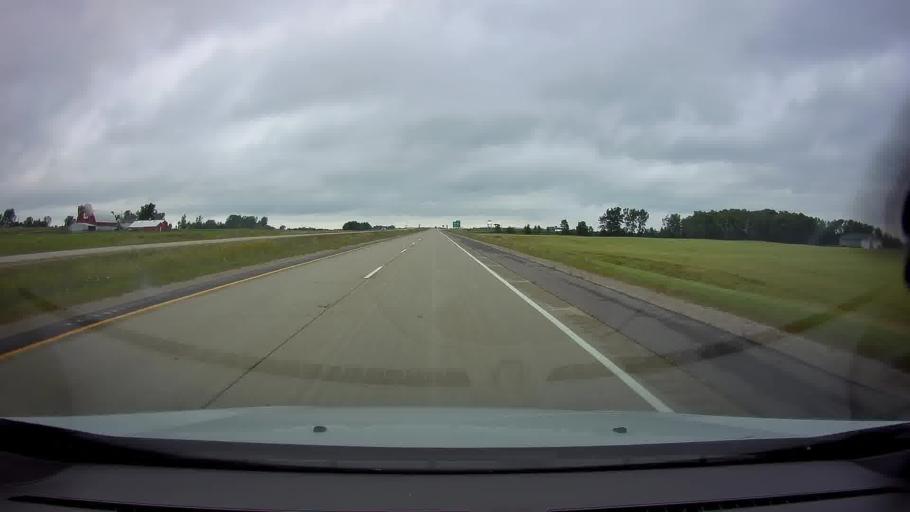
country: US
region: Wisconsin
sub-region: Brown County
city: Pulaski
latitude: 44.6658
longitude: -88.3054
